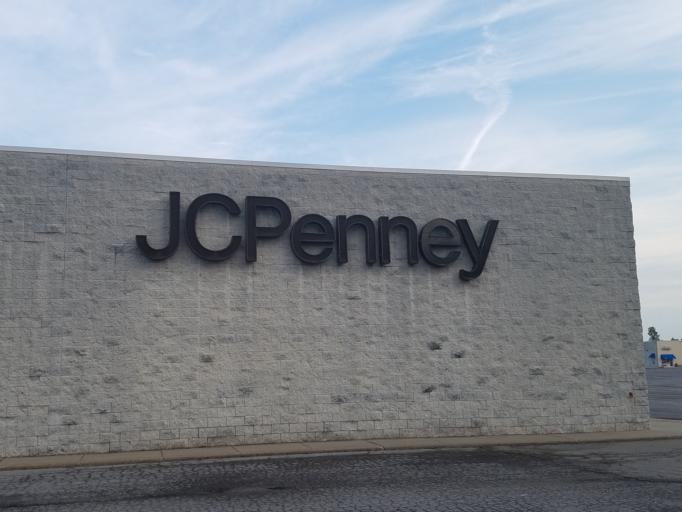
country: US
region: Pennsylvania
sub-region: Clarion County
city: Clarion
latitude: 41.1927
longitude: -79.3933
